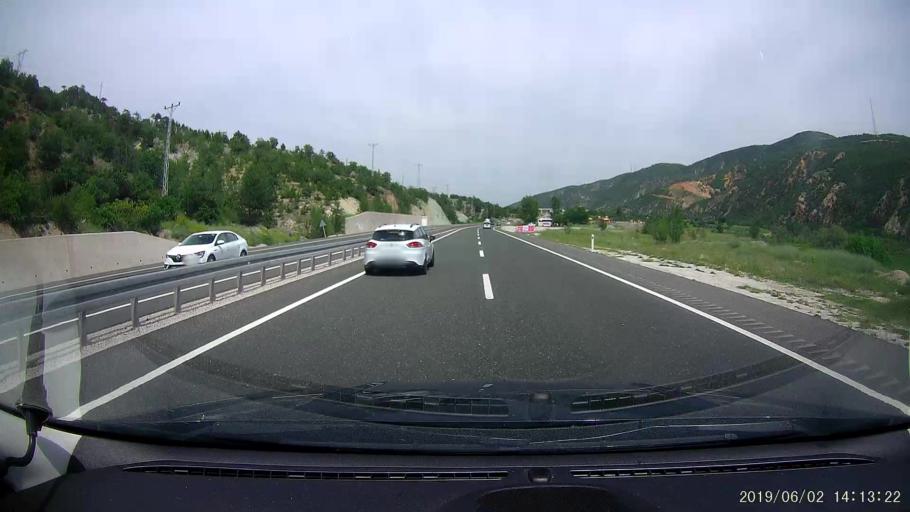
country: TR
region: Cankiri
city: Yaprakli
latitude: 40.9255
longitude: 33.8278
